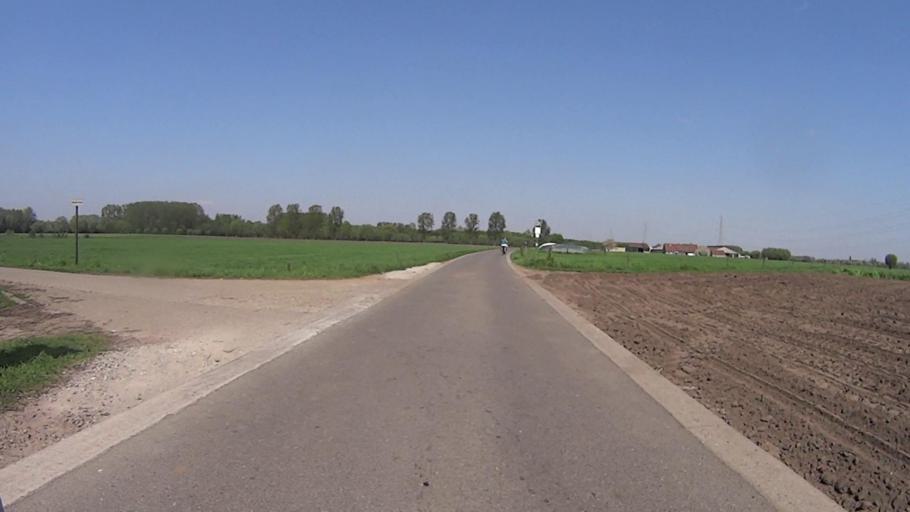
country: BE
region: Flanders
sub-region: Provincie Antwerpen
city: Sint-Amands
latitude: 51.0613
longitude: 4.2160
